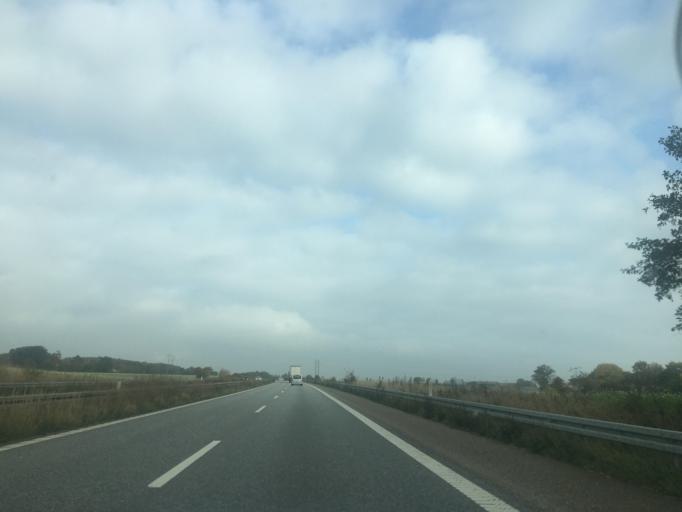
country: DK
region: Zealand
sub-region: Guldborgsund Kommune
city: Norre Alslev
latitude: 54.8731
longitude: 11.8923
